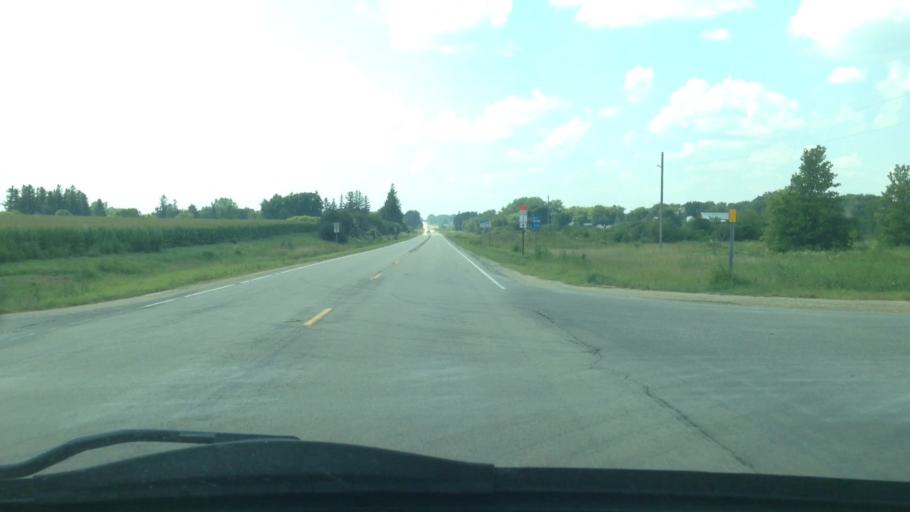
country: US
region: Minnesota
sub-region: Olmsted County
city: Stewartville
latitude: 43.8555
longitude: -92.4383
